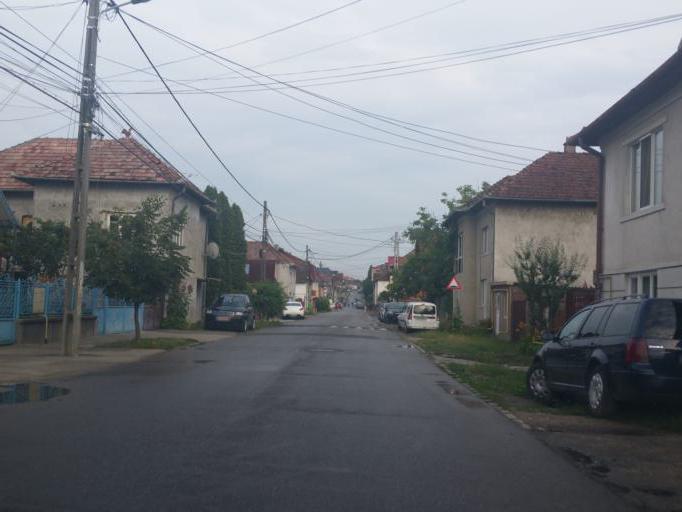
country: RO
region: Cluj
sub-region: Comuna Baciu
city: Baciu
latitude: 46.7953
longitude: 23.5231
